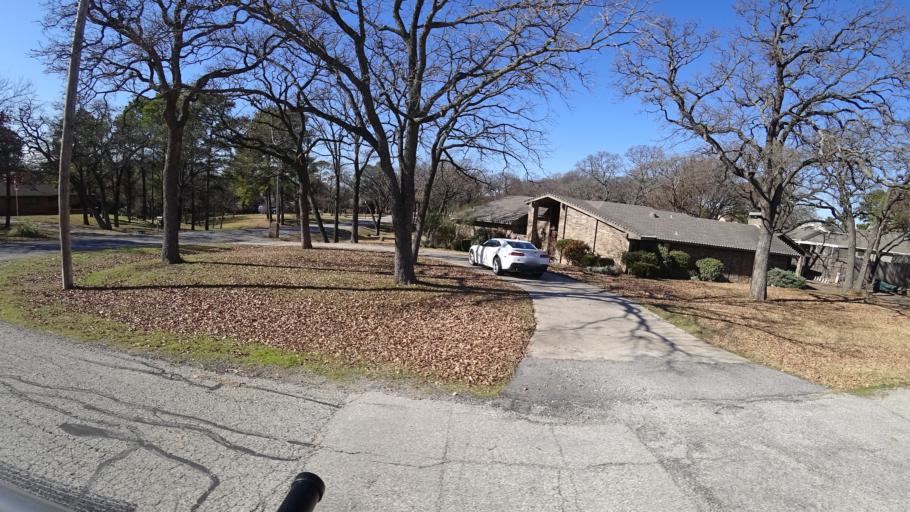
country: US
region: Texas
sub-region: Denton County
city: Lewisville
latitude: 33.0236
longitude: -97.0154
